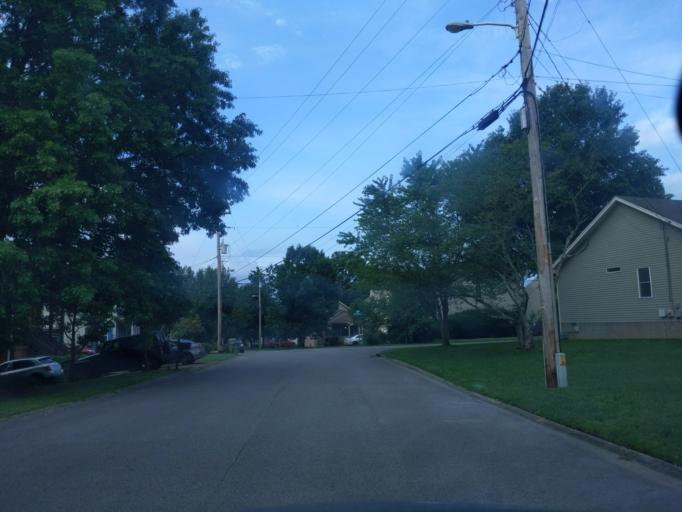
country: US
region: Tennessee
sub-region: Wilson County
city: Green Hill
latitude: 36.1857
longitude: -86.5963
